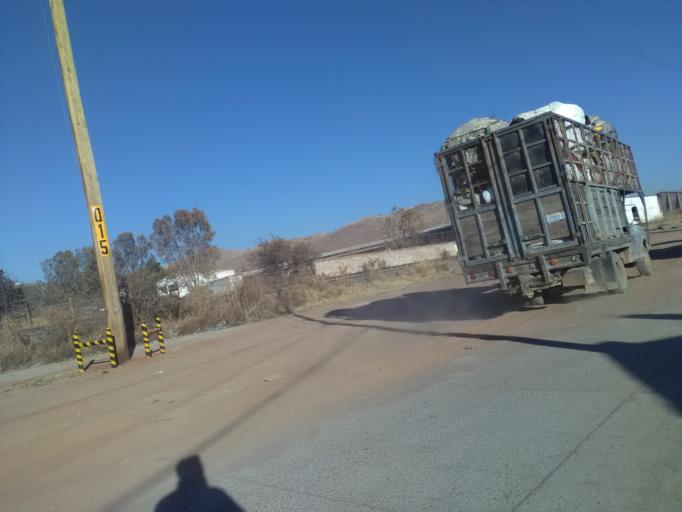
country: MX
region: Durango
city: Victoria de Durango
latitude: 24.0568
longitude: -104.6544
